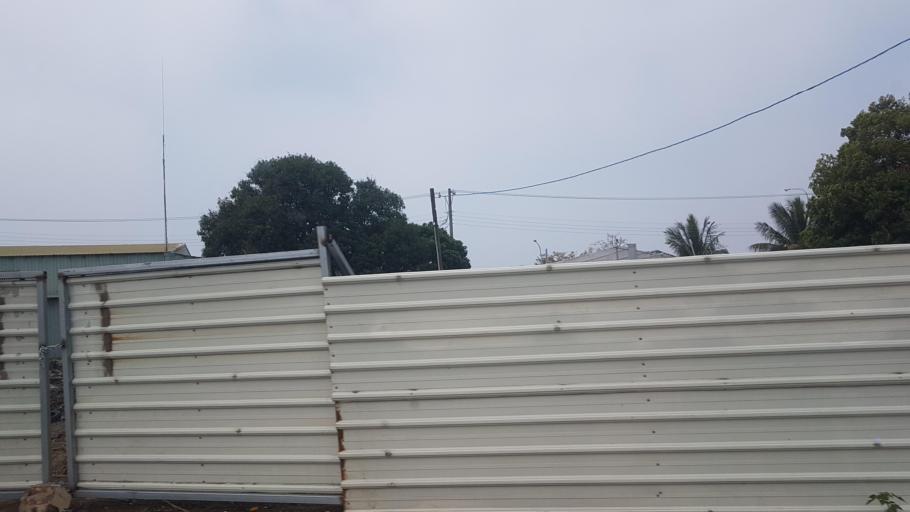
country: TW
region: Taiwan
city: Xinying
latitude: 23.3074
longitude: 120.2937
